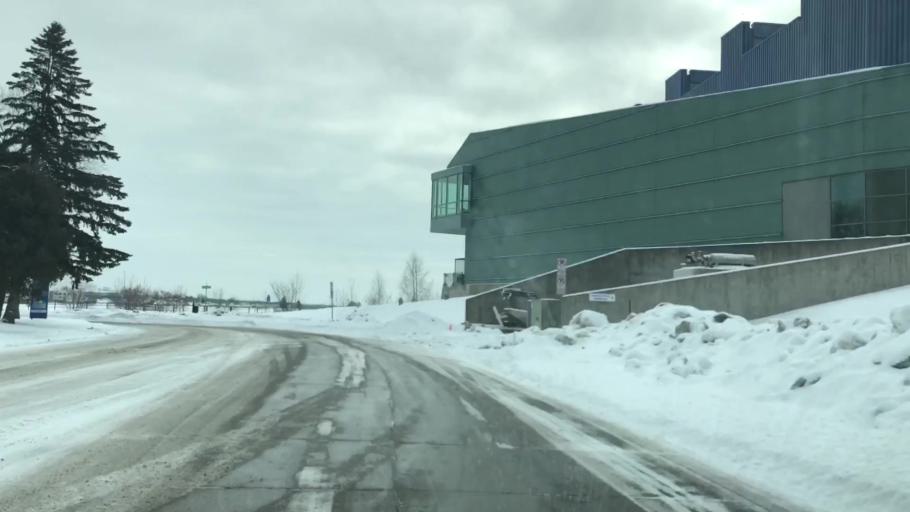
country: US
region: Minnesota
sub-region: Saint Louis County
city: Duluth
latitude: 46.7796
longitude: -92.0999
